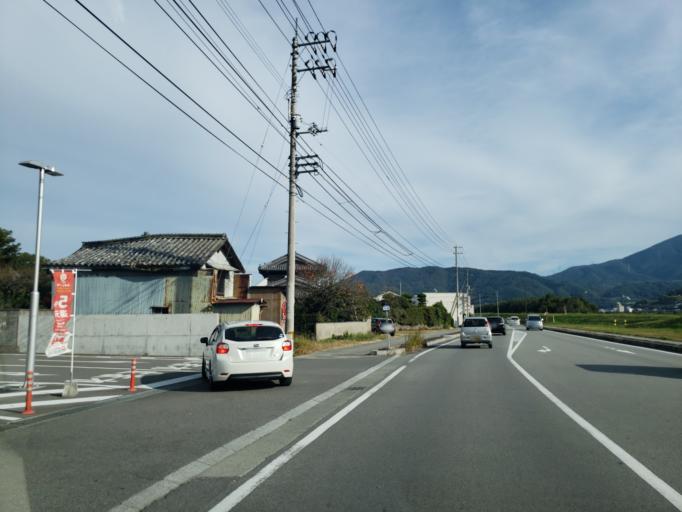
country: JP
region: Tokushima
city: Wakimachi
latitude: 34.0657
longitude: 134.1496
